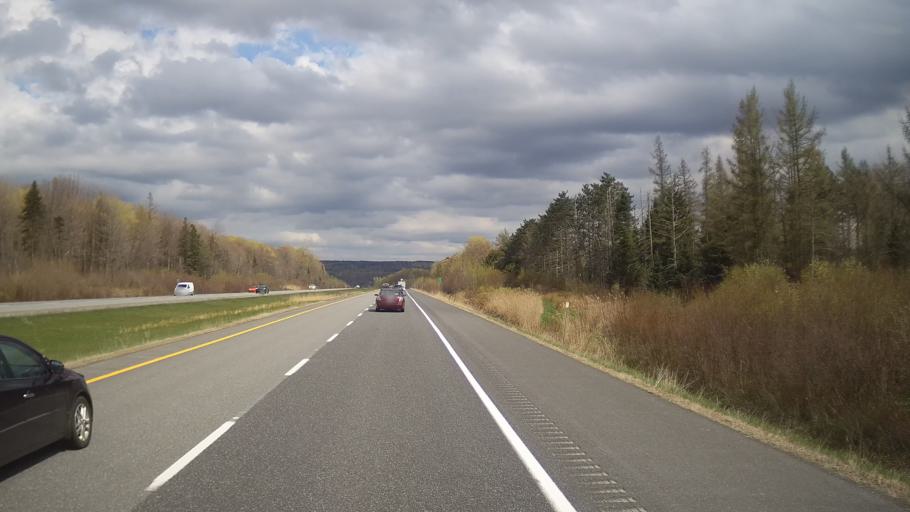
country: CA
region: Quebec
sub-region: Monteregie
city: Waterloo
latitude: 45.3032
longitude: -72.4697
